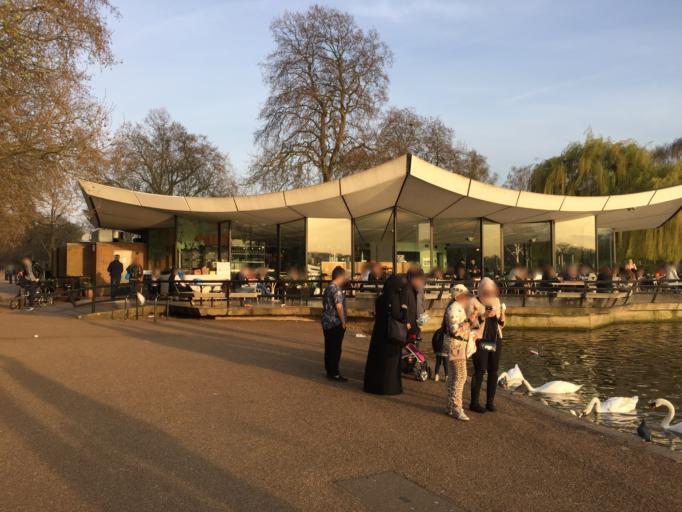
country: GB
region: England
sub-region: Greater London
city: Chelsea
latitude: 51.5053
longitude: -0.1602
